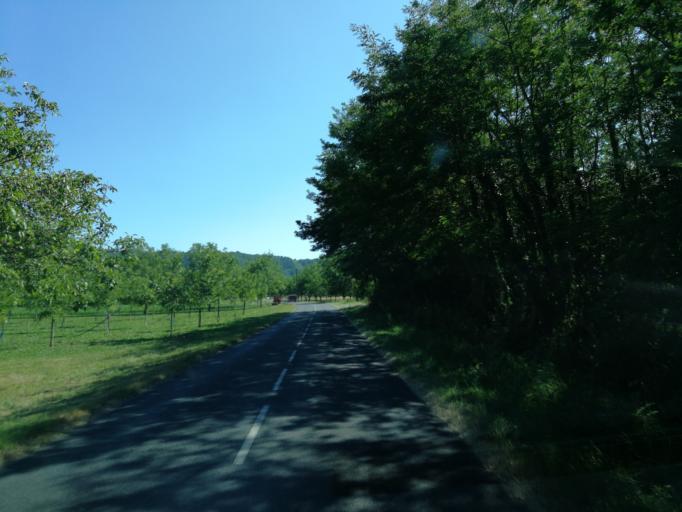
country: FR
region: Midi-Pyrenees
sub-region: Departement du Lot
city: Souillac
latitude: 44.8789
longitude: 1.4465
